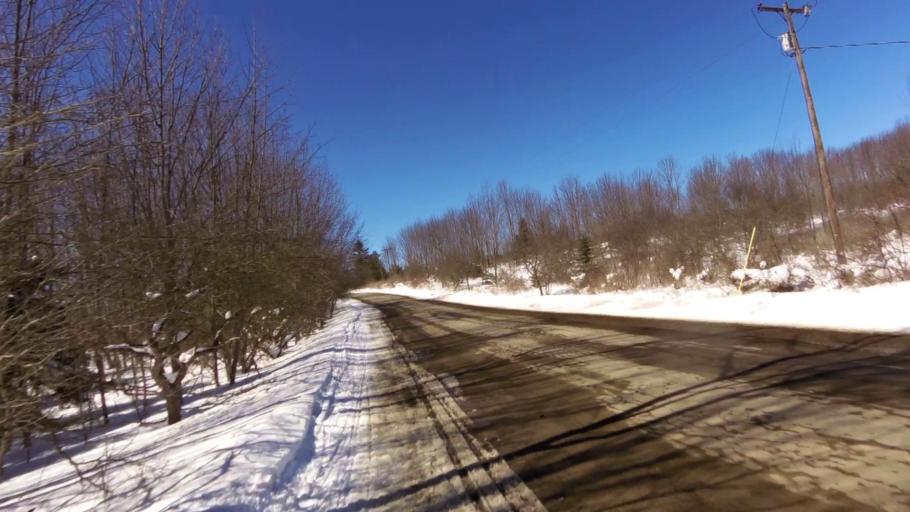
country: US
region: New York
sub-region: Allegany County
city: Houghton
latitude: 42.4131
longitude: -78.3045
